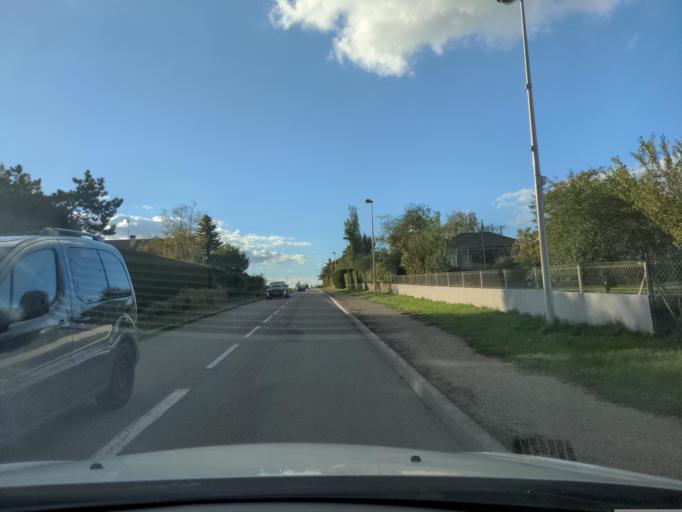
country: FR
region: Bourgogne
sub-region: Departement de la Cote-d'Or
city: Ruffey-les-Echirey
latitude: 47.3813
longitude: 5.0638
